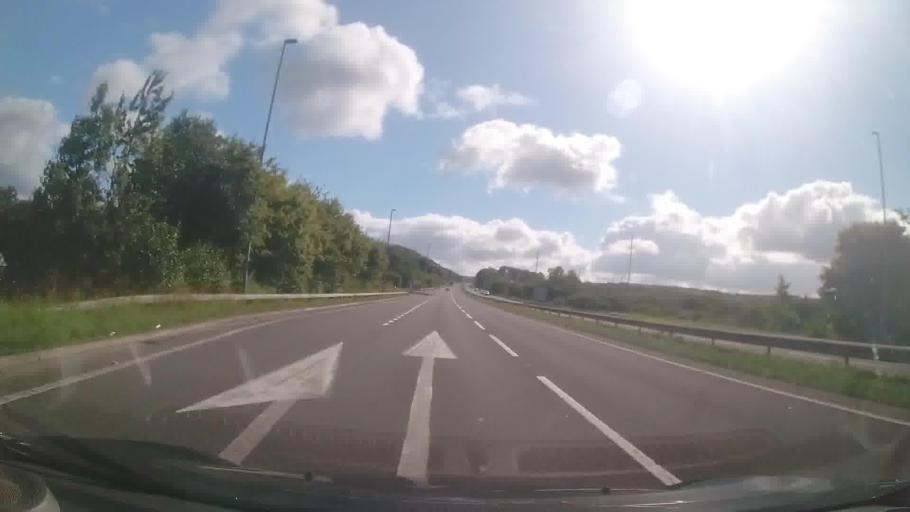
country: GB
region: Wales
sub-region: Carmarthenshire
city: Llanddarog
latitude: 51.8293
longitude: -4.1515
